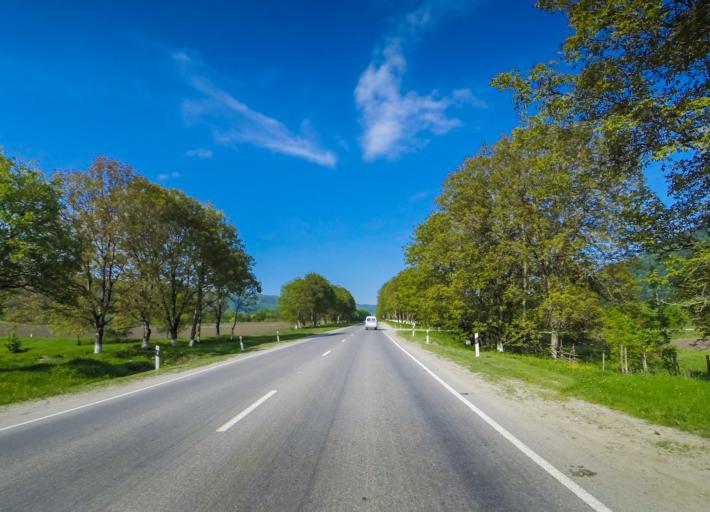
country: RU
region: Kabardino-Balkariya
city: Kashkhatau
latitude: 43.3036
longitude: 43.5863
